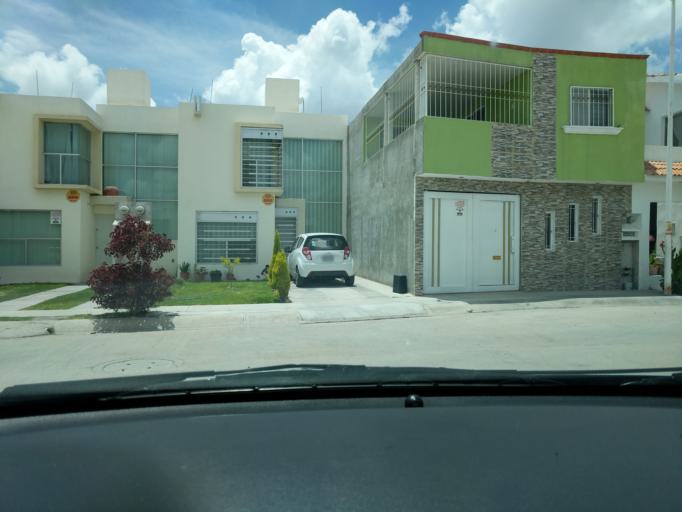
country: MX
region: San Luis Potosi
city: Soledad Diez Gutierrez
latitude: 22.2160
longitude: -100.9381
